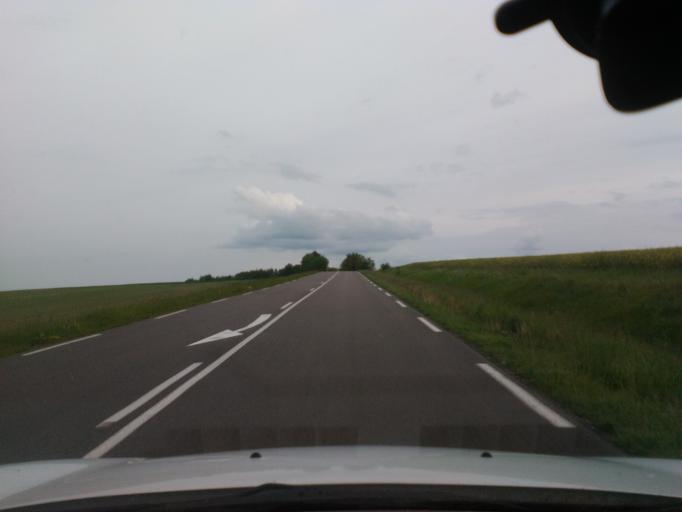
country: FR
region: Champagne-Ardenne
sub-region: Departement de la Haute-Marne
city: Lavilleneuve-au-Roi
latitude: 48.1983
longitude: 4.9451
